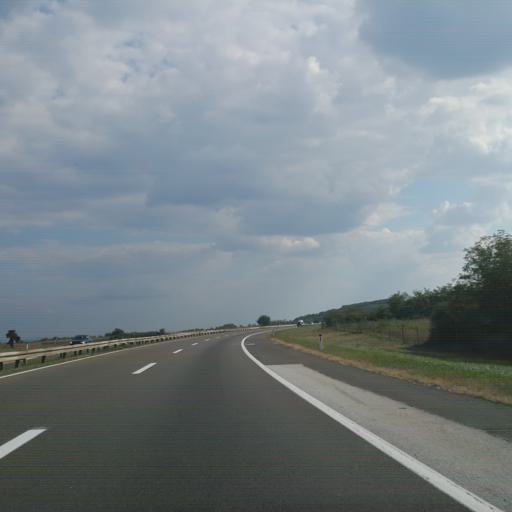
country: RS
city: Lugavcina
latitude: 44.5371
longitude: 20.9988
